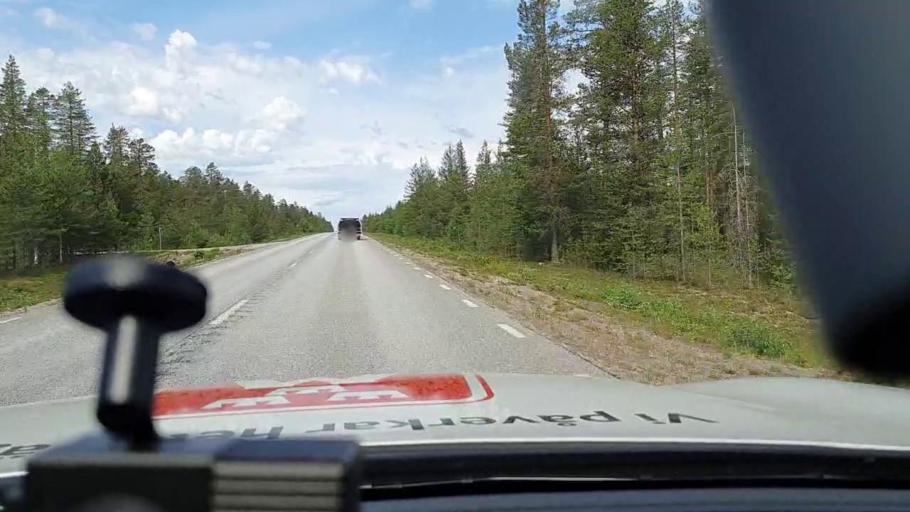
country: SE
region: Norrbotten
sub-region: Jokkmokks Kommun
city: Jokkmokk
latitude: 66.5245
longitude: 20.2004
